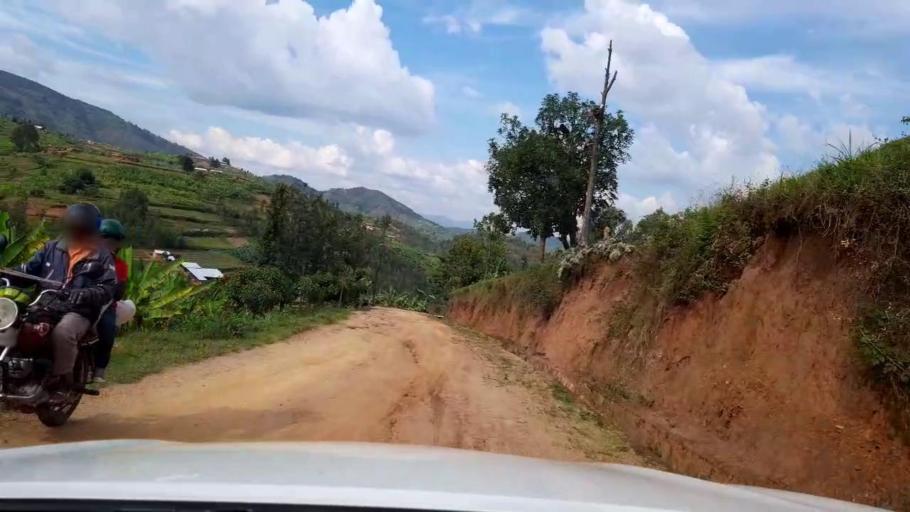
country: RW
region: Southern Province
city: Gitarama
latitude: -1.9763
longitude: 29.7088
